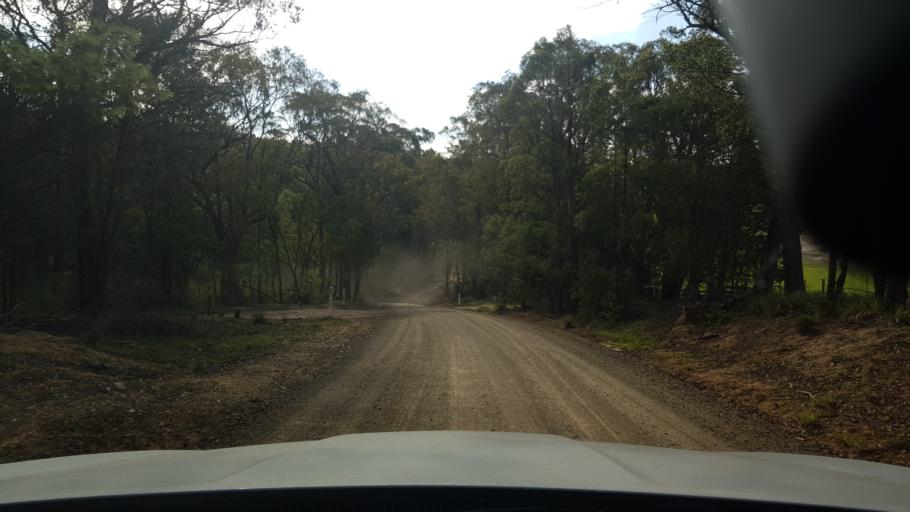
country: AU
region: Victoria
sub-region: East Gippsland
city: Bairnsdale
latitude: -37.7702
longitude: 147.5677
